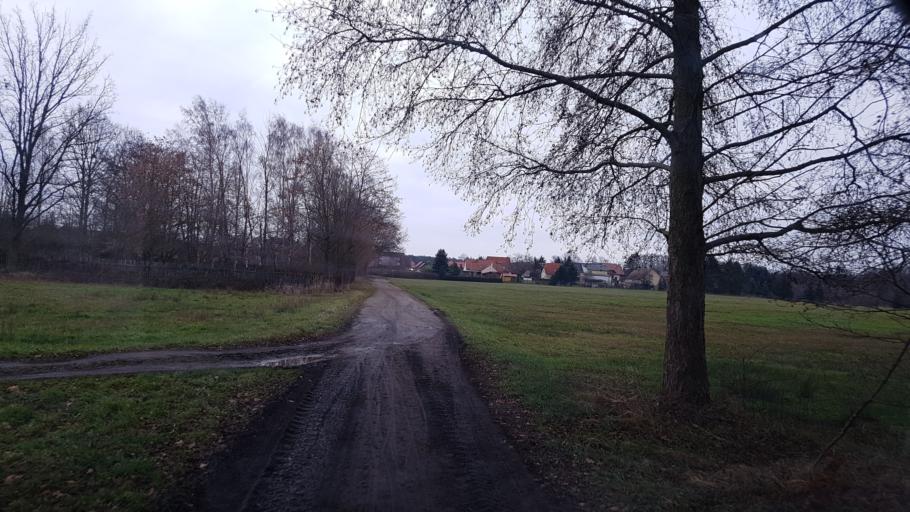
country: DE
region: Brandenburg
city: Doberlug-Kirchhain
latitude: 51.6094
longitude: 13.5932
